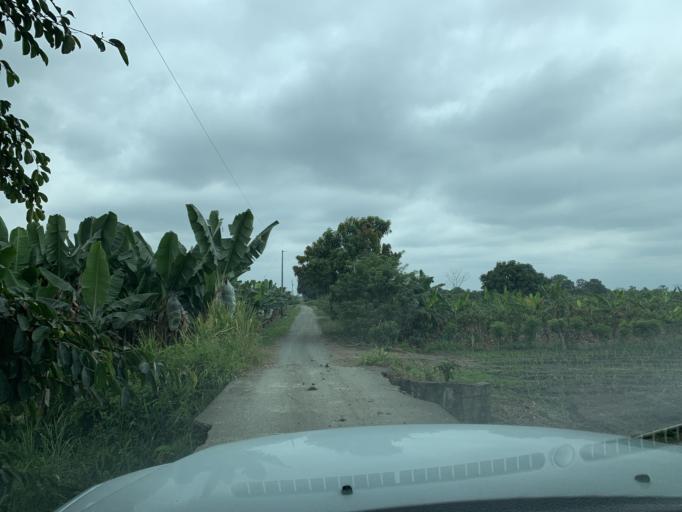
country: EC
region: Guayas
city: Coronel Marcelino Mariduena
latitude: -2.3433
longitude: -79.4583
